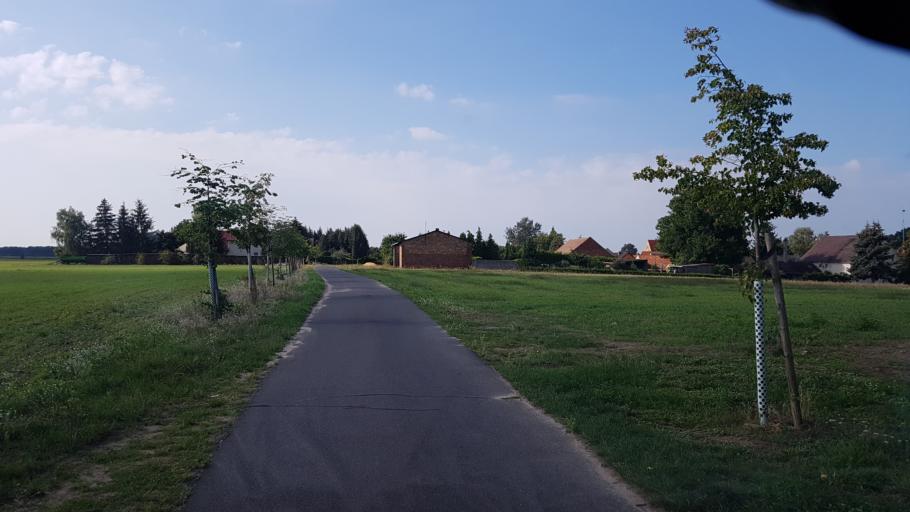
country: DE
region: Brandenburg
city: Luebben
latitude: 51.8845
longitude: 13.8474
